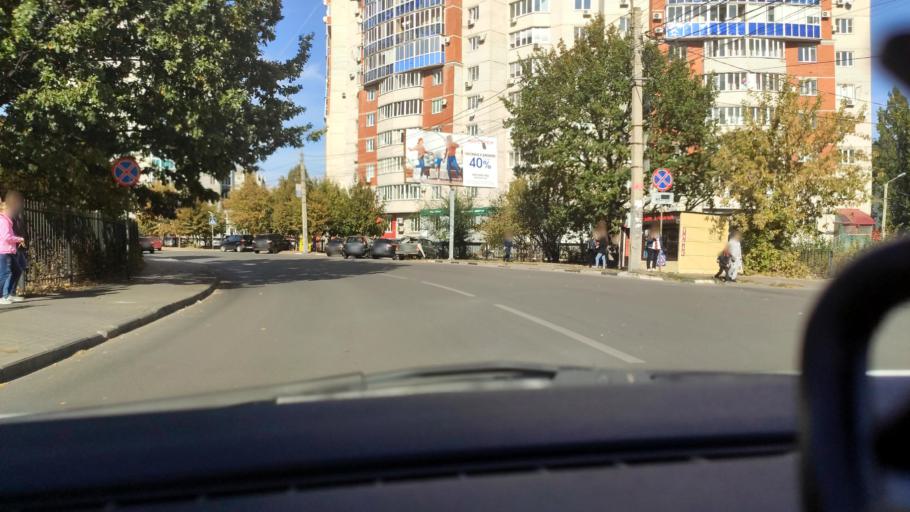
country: RU
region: Voronezj
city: Podgornoye
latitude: 51.7166
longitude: 39.1749
